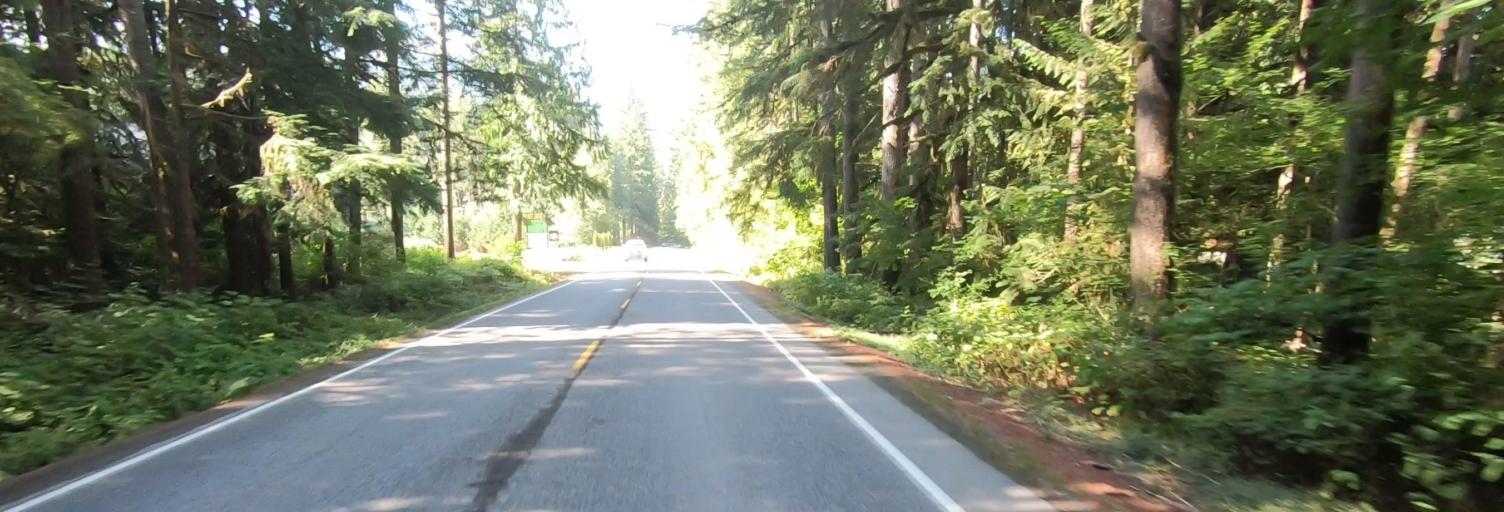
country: US
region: Washington
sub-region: Whatcom County
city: Peaceful Valley
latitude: 48.8951
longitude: -121.9362
